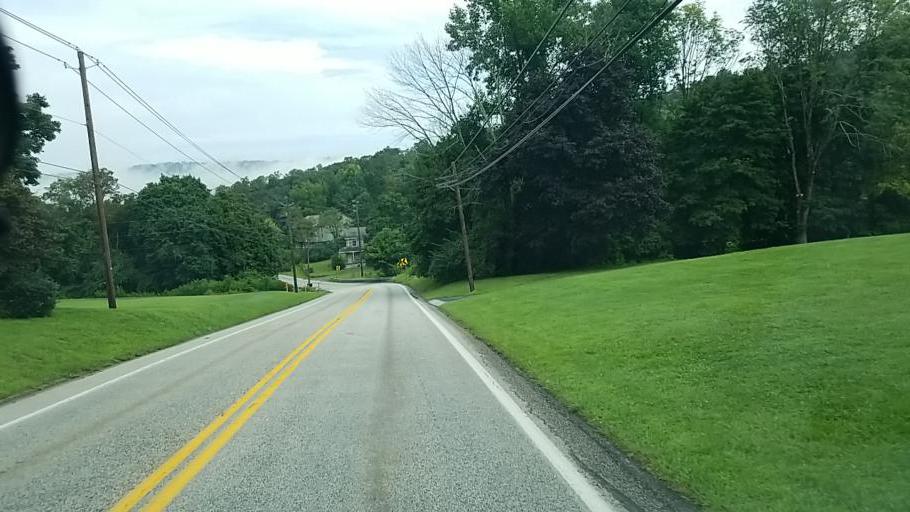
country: US
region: Pennsylvania
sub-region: Perry County
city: Marysville
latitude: 40.3821
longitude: -76.9337
